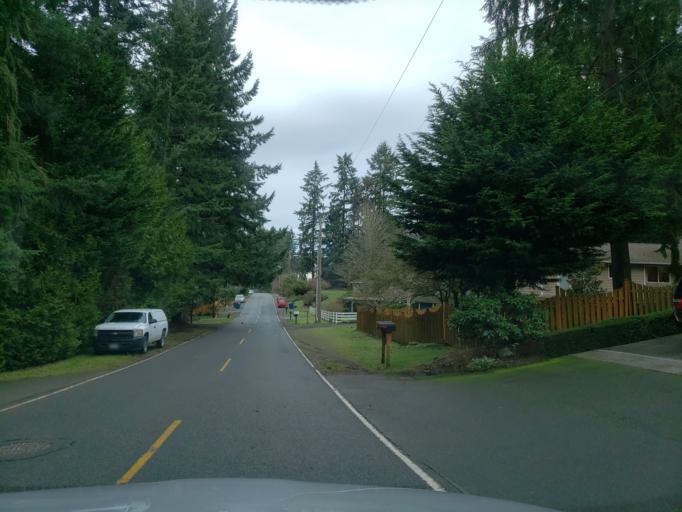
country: US
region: Washington
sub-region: Snohomish County
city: Lynnwood
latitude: 47.8151
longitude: -122.3426
